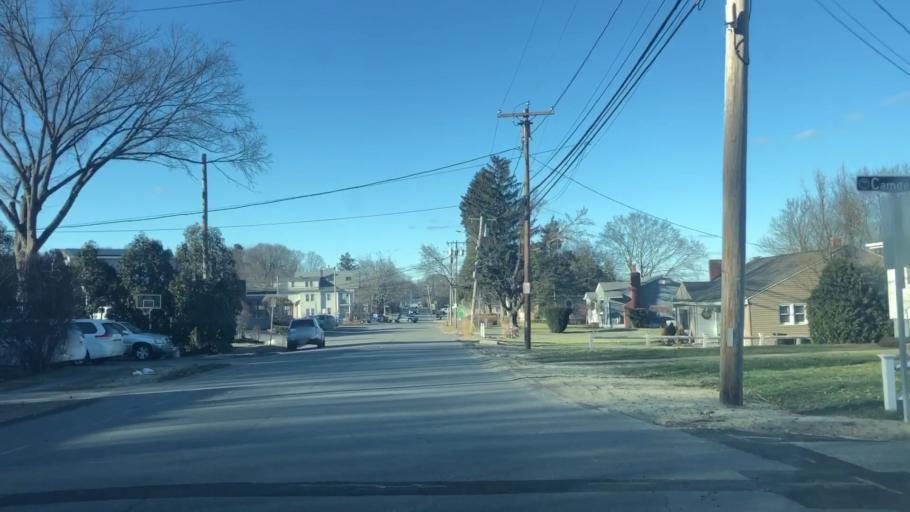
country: US
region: Massachusetts
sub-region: Essex County
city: North Andover
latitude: 42.6944
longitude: -71.1181
